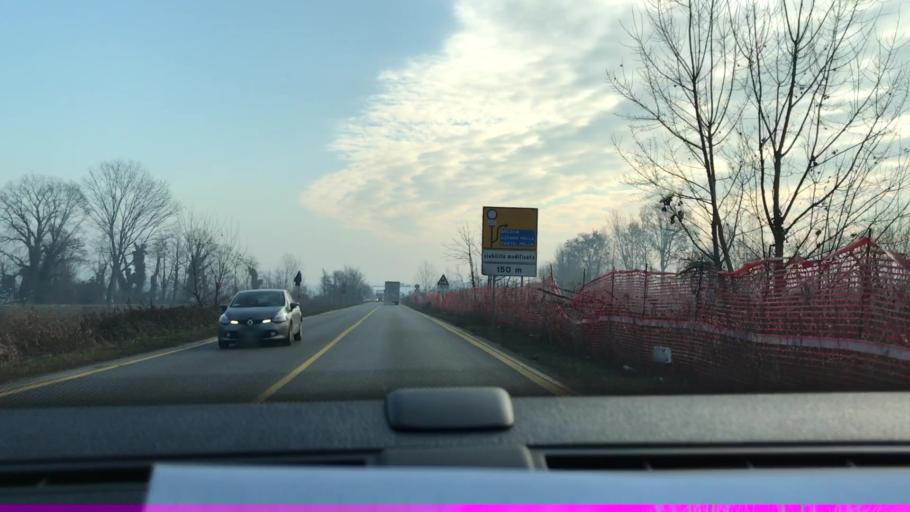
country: IT
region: Lombardy
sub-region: Provincia di Brescia
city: Capriano del Colle
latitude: 45.4845
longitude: 10.1142
